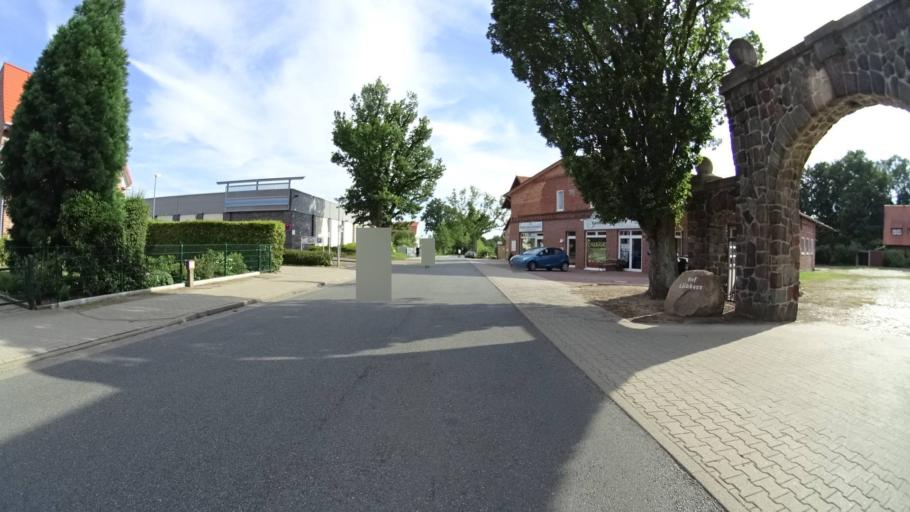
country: DE
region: Lower Saxony
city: Reppenstedt
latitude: 53.2472
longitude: 10.3595
